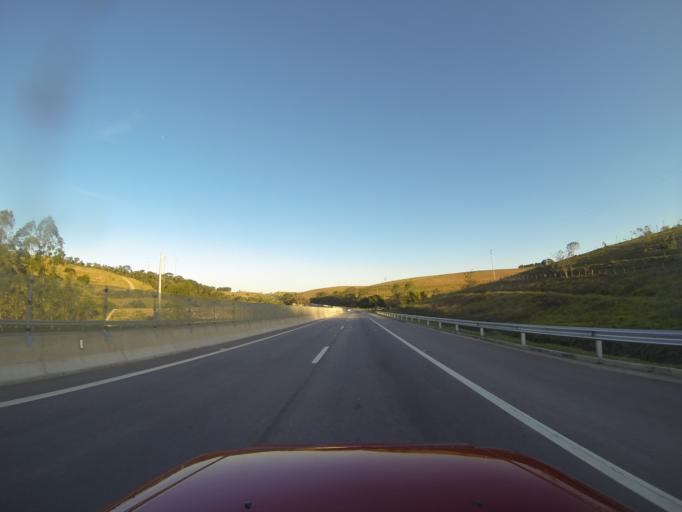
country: BR
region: Sao Paulo
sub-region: Santa Branca
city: Santa Branca
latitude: -23.4288
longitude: -45.6278
